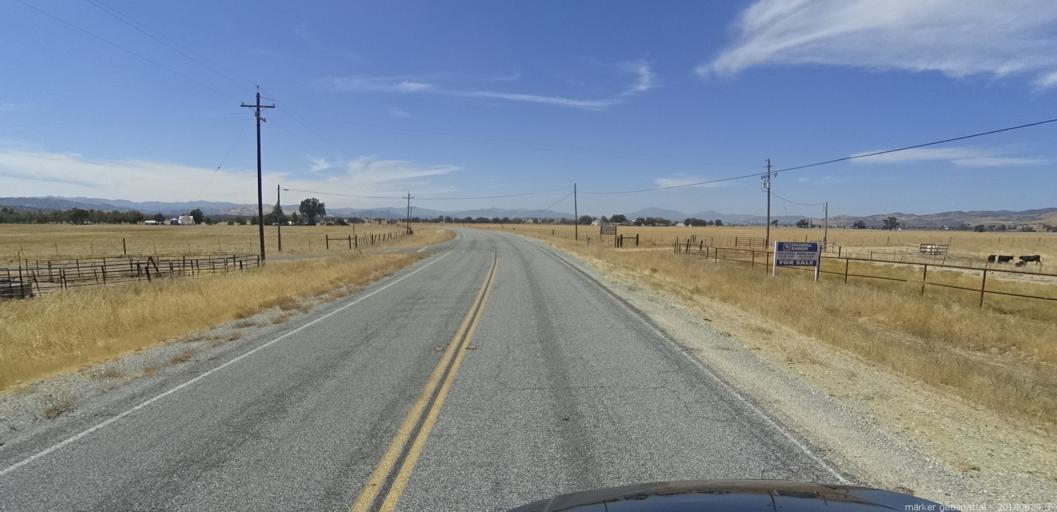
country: US
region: California
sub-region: San Luis Obispo County
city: Lake Nacimiento
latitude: 35.9362
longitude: -121.0635
